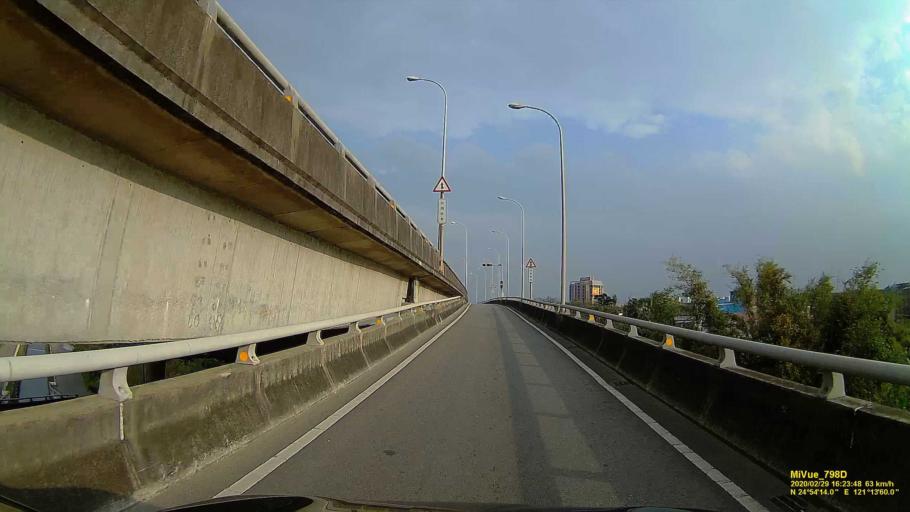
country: TW
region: Taiwan
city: Daxi
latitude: 24.9037
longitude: 121.2335
